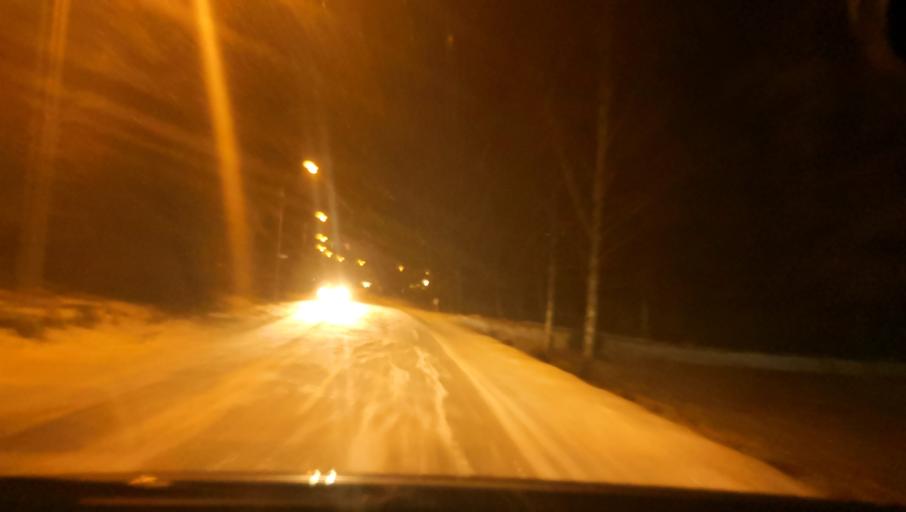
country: SE
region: Uppsala
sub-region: Heby Kommun
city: Tarnsjo
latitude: 60.1465
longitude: 16.9151
